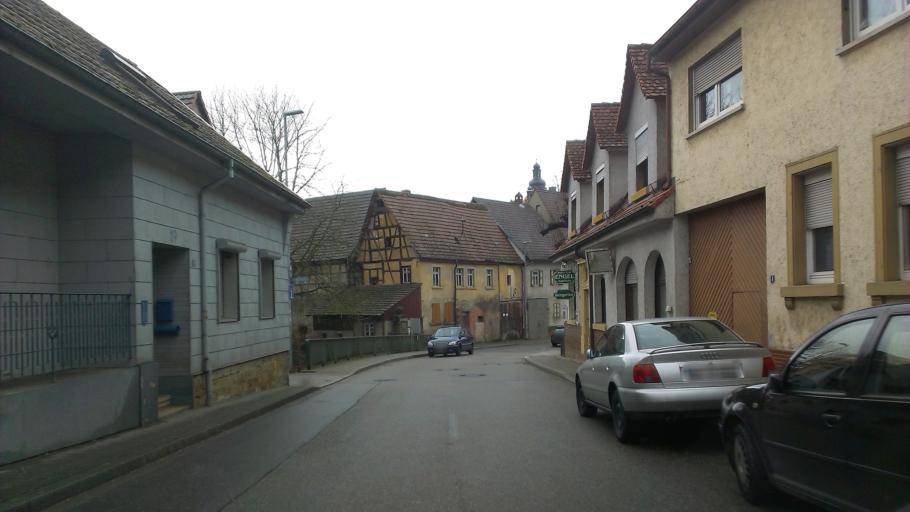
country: DE
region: Baden-Wuerttemberg
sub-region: Karlsruhe Region
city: Zaisenhausen
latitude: 49.1032
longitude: 8.7514
